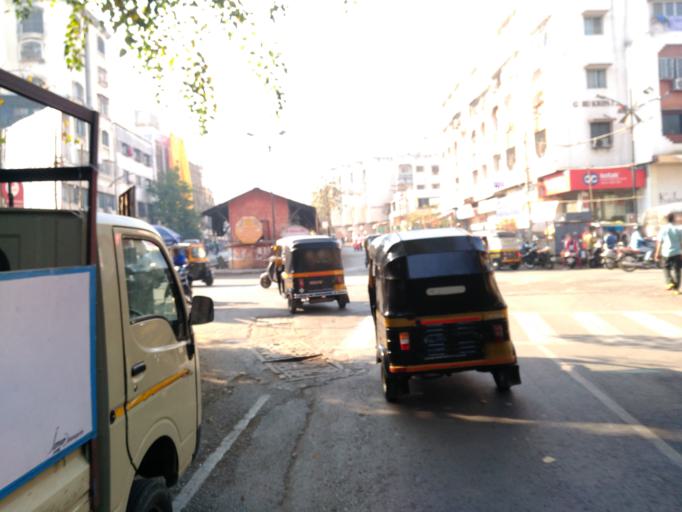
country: IN
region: Maharashtra
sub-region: Pune Division
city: Pune
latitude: 18.5096
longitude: 73.8723
